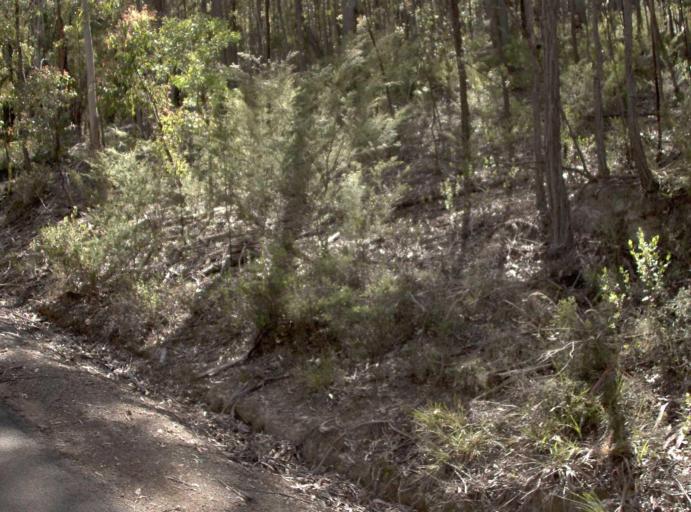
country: AU
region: Victoria
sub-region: East Gippsland
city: Lakes Entrance
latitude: -37.4389
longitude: 148.1326
